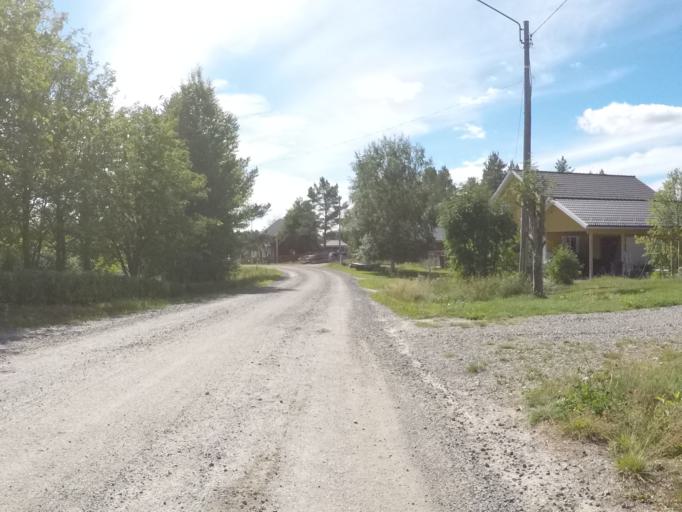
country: SE
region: Vaesterbotten
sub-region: Robertsfors Kommun
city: Robertsfors
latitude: 64.0018
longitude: 20.8112
